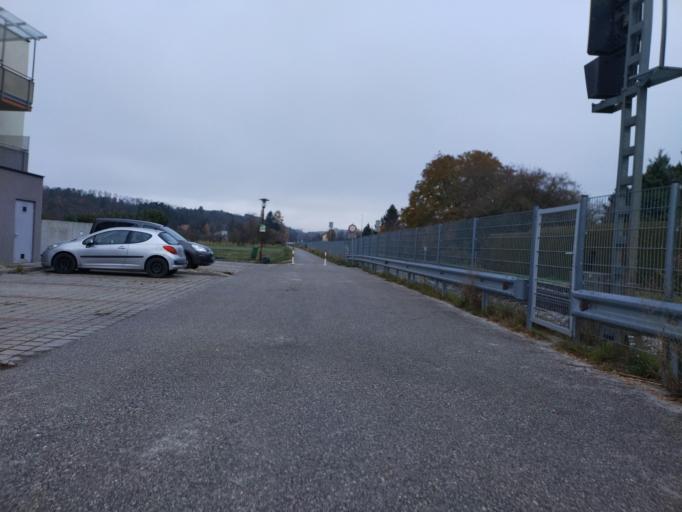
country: AT
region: Lower Austria
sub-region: Politischer Bezirk Neunkirchen
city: Pitten
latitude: 47.7138
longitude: 16.1770
